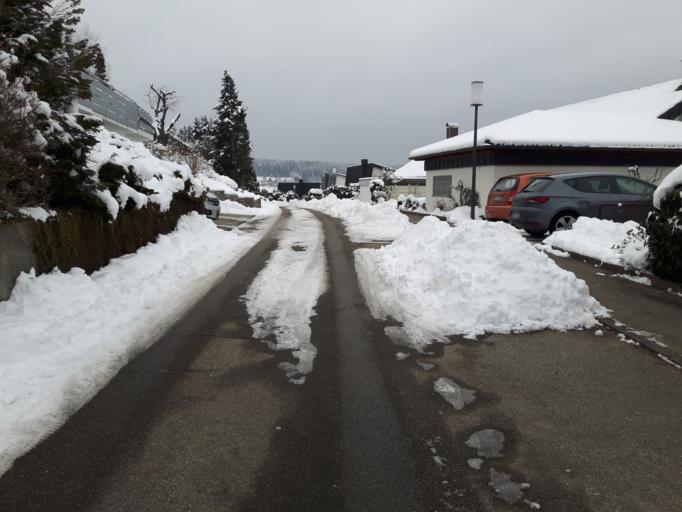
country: DE
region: Baden-Wuerttemberg
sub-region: Freiburg Region
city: Unterkirnach
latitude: 48.0823
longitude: 8.3607
